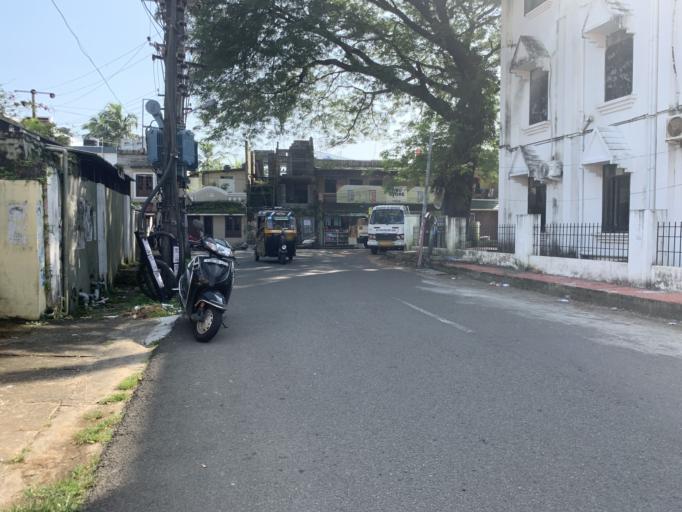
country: IN
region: Kerala
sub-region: Ernakulam
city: Cochin
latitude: 9.9603
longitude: 76.2567
